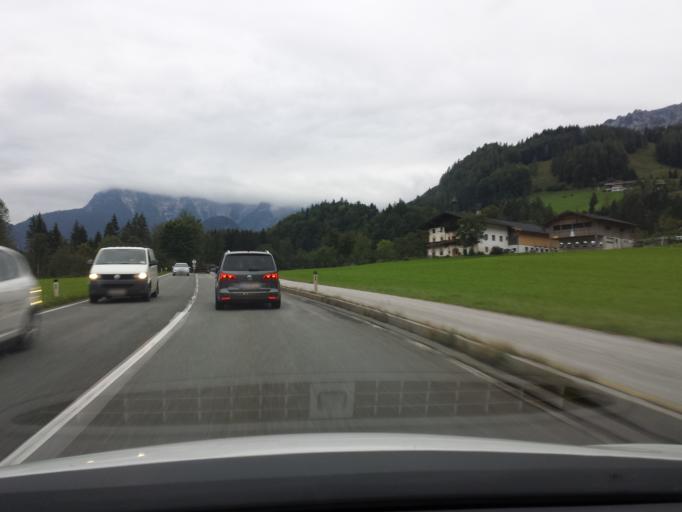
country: AT
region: Salzburg
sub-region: Politischer Bezirk Zell am See
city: Lofer
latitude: 47.6117
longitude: 12.7034
